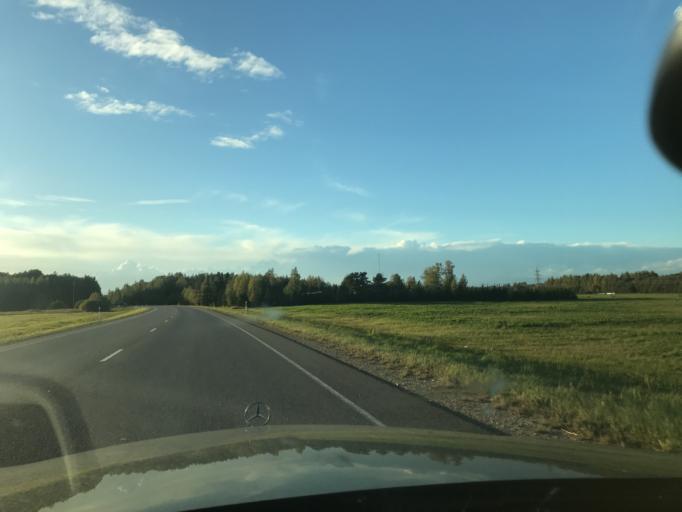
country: EE
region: Vorumaa
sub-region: Voru linn
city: Voru
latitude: 57.8578
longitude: 27.0161
